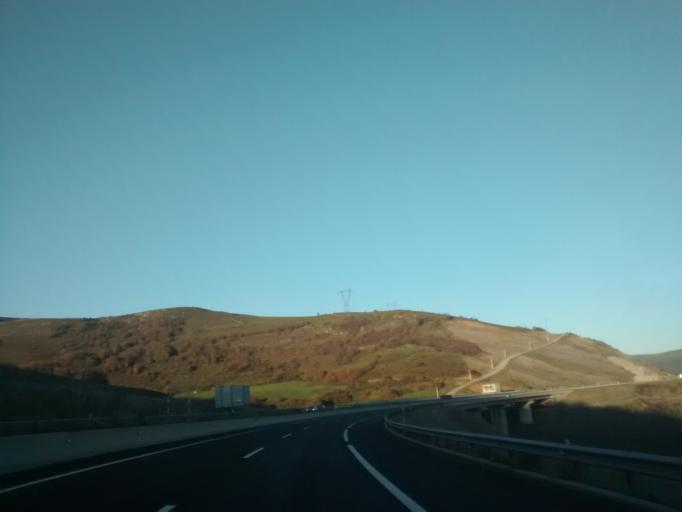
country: ES
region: Cantabria
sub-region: Provincia de Cantabria
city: Reinosa
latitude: 43.0191
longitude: -4.1243
